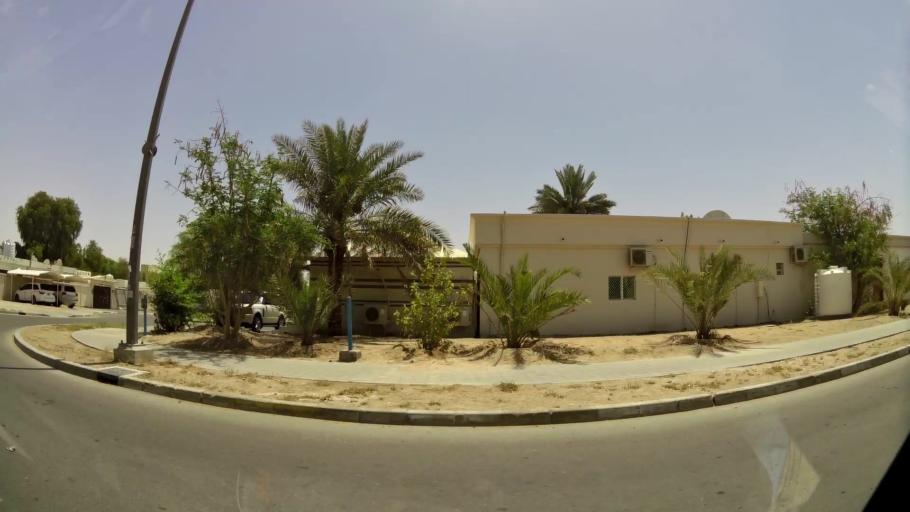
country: OM
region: Al Buraimi
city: Al Buraymi
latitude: 24.2717
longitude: 55.7460
